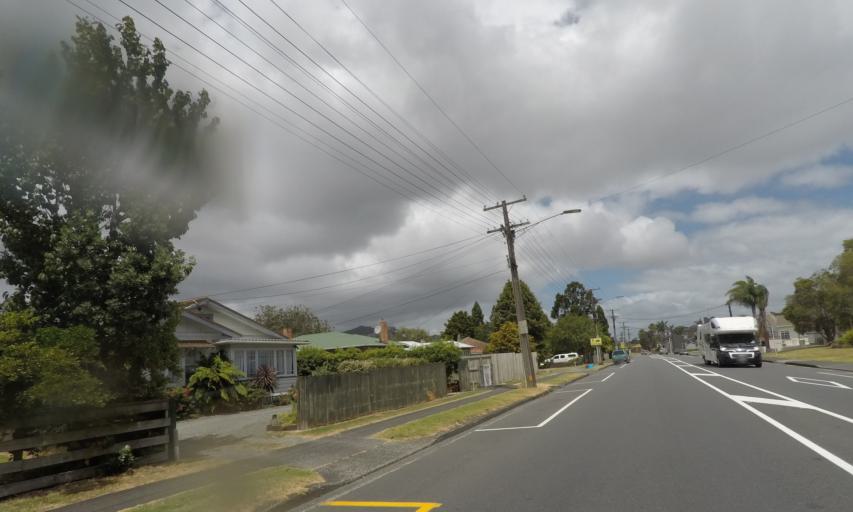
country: NZ
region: Northland
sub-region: Whangarei
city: Whangarei
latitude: -35.7013
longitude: 174.3148
